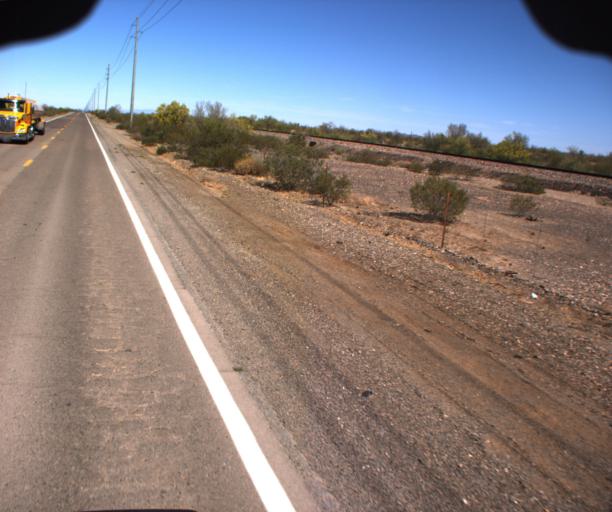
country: US
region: Arizona
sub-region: La Paz County
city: Salome
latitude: 33.7776
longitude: -113.8025
